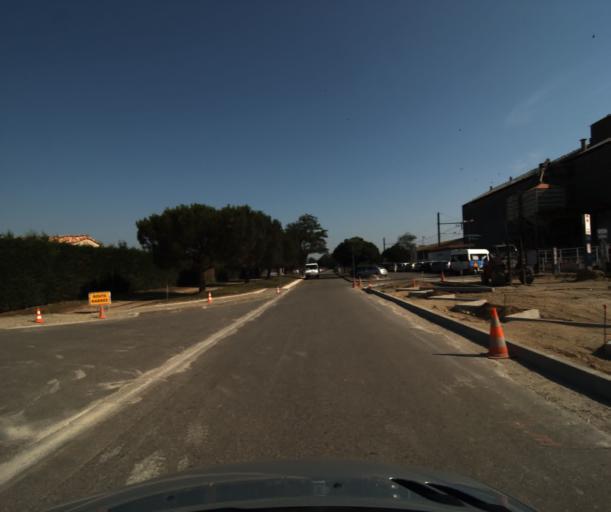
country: FR
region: Midi-Pyrenees
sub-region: Departement de la Haute-Garonne
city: Lacroix-Falgarde
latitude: 43.4798
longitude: 1.3996
